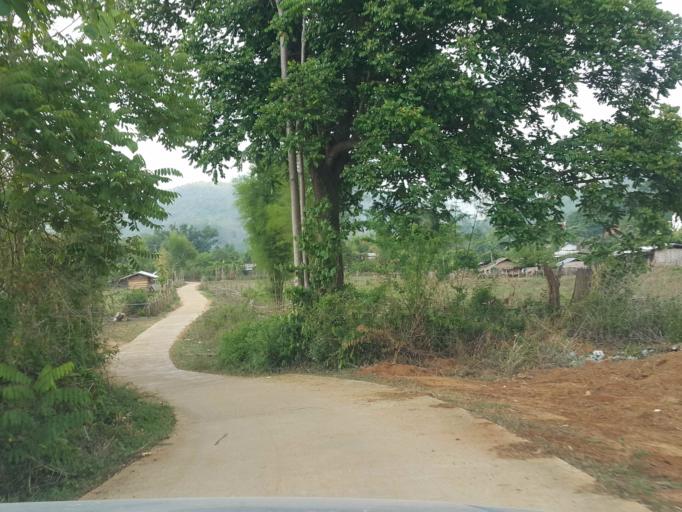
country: TH
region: Chiang Mai
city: Wiang Haeng
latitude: 19.3746
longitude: 98.7208
